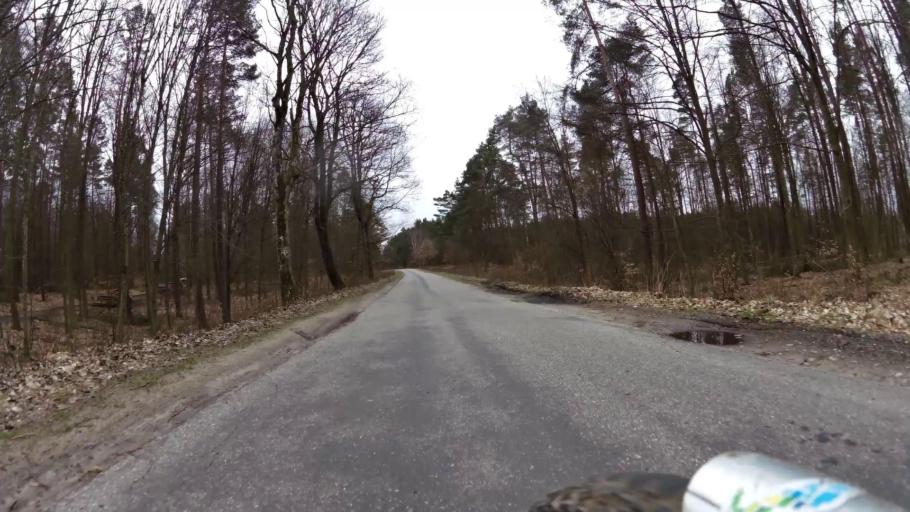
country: PL
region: Pomeranian Voivodeship
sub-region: Powiat bytowski
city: Trzebielino
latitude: 54.0970
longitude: 17.1343
